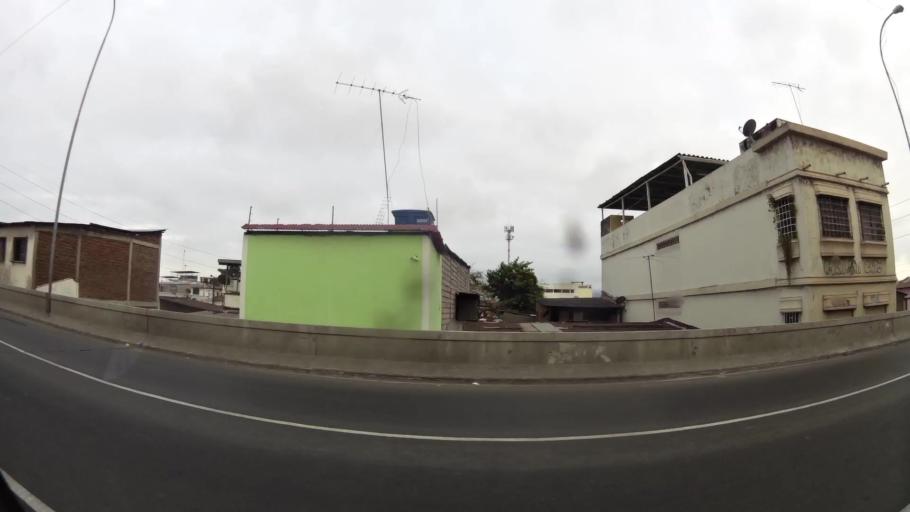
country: EC
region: Guayas
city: Guayaquil
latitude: -2.2076
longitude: -79.8965
